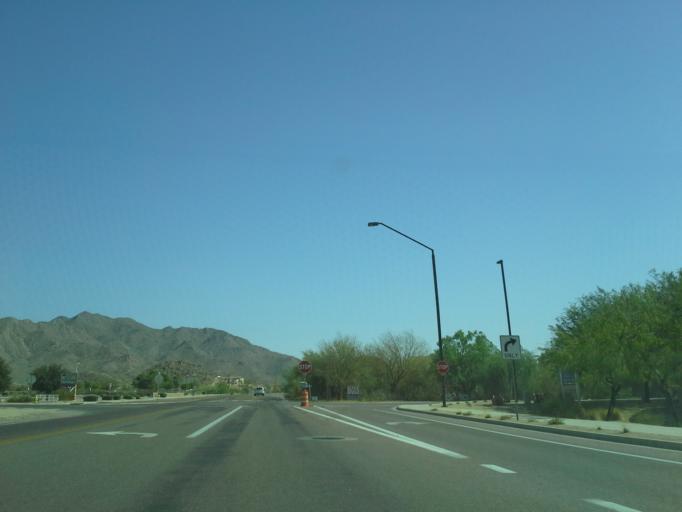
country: US
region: Arizona
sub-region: Maricopa County
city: Queen Creek
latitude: 33.2125
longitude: -111.7205
